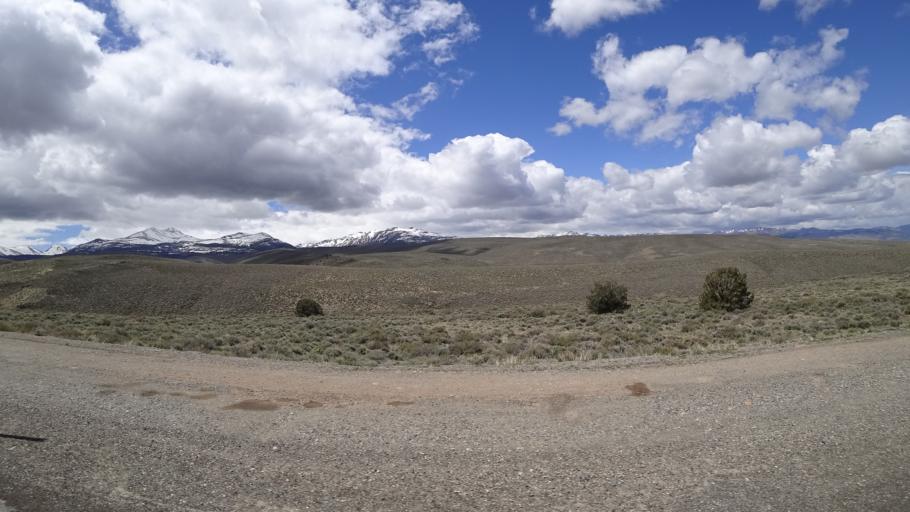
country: US
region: California
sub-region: Mono County
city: Bridgeport
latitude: 38.1455
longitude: -119.1849
